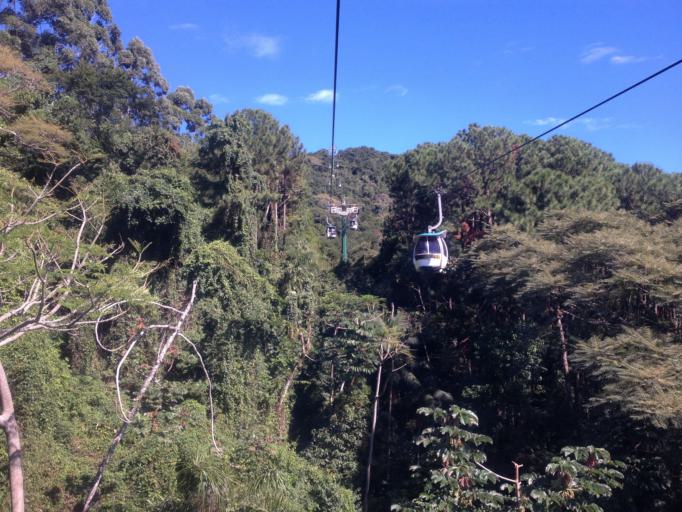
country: BR
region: Santa Catarina
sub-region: Balneario Camboriu
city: Balneario Camboriu
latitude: -26.9990
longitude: -48.5916
